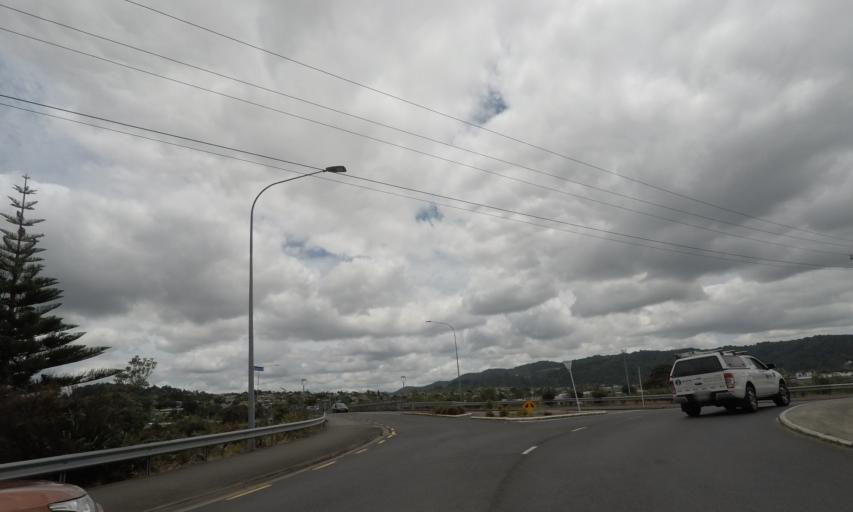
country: NZ
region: Northland
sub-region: Whangarei
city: Whangarei
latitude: -35.7336
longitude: 174.3274
